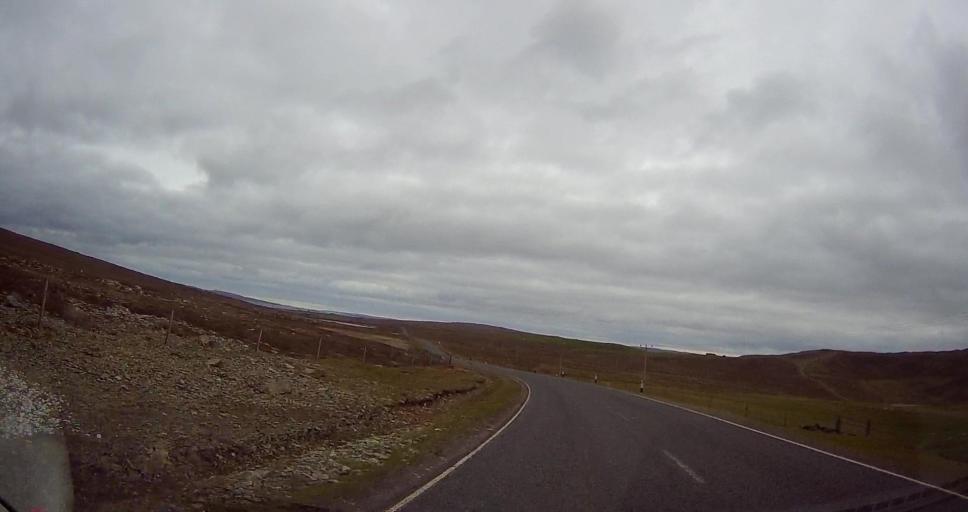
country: GB
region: Scotland
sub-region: Shetland Islands
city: Shetland
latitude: 60.7238
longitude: -0.9074
